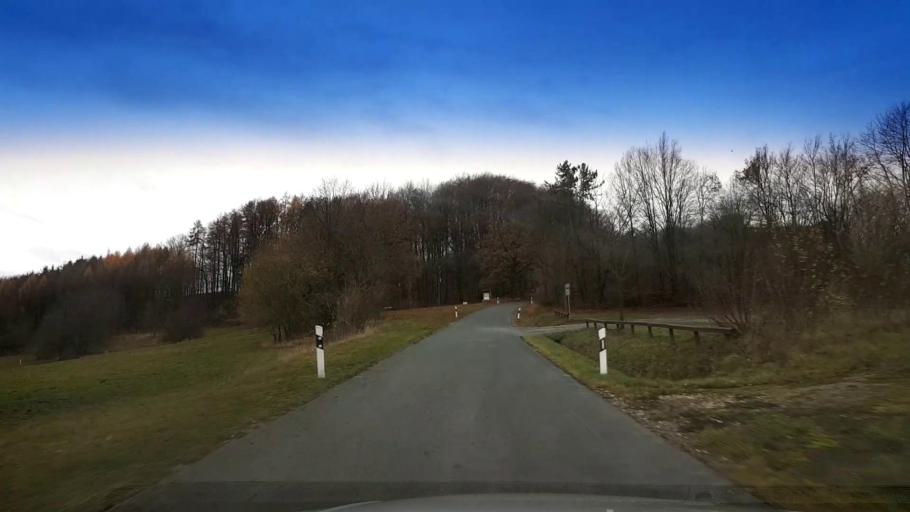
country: DE
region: Bavaria
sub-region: Upper Franconia
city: Schesslitz
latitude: 49.9600
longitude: 11.0525
